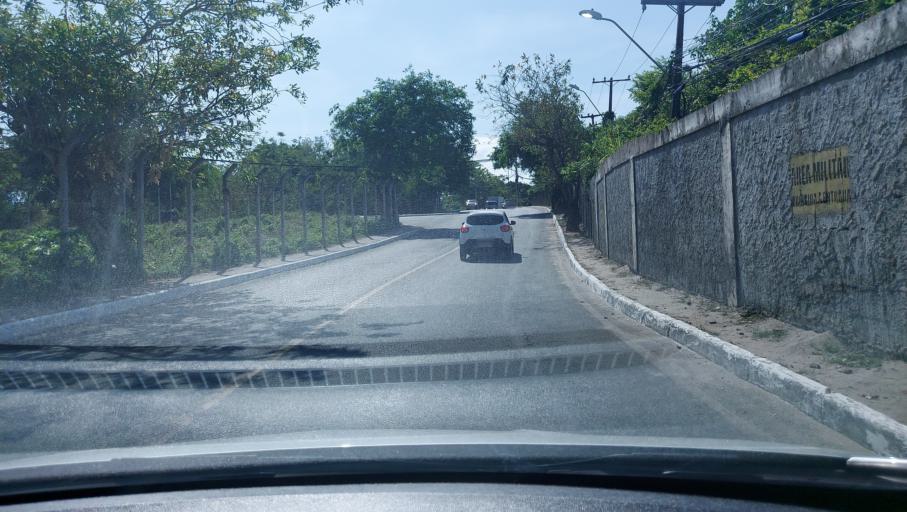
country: BR
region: Bahia
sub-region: Salvador
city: Salvador
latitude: -12.9782
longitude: -38.4430
